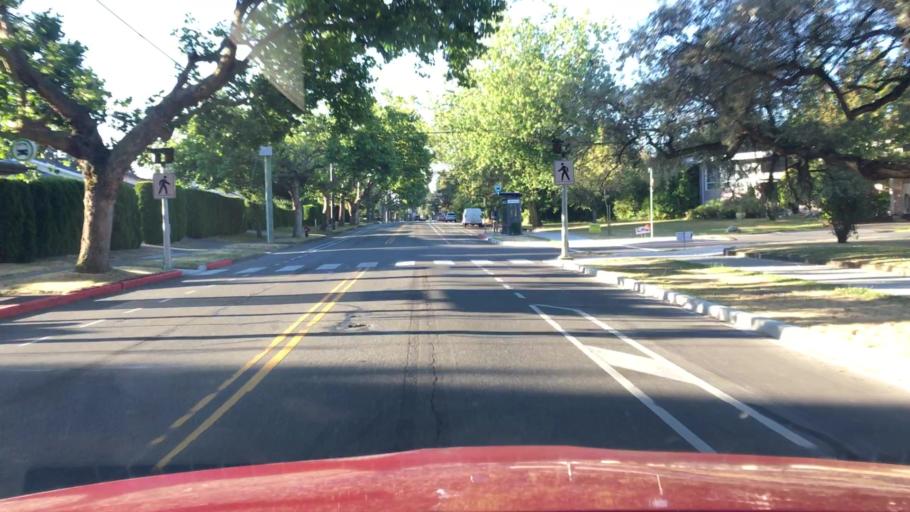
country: CA
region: British Columbia
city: Oak Bay
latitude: 48.4801
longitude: -123.3358
